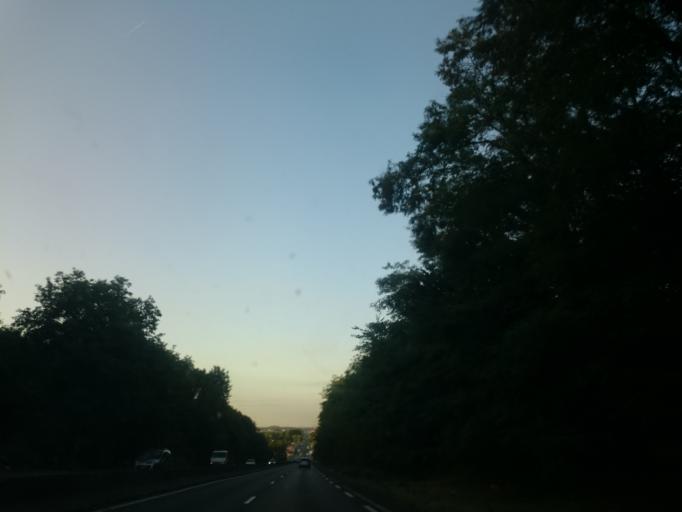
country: FR
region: Ile-de-France
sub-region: Departement de l'Essonne
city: Boissy-sous-Saint-Yon
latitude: 48.5397
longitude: 2.2103
